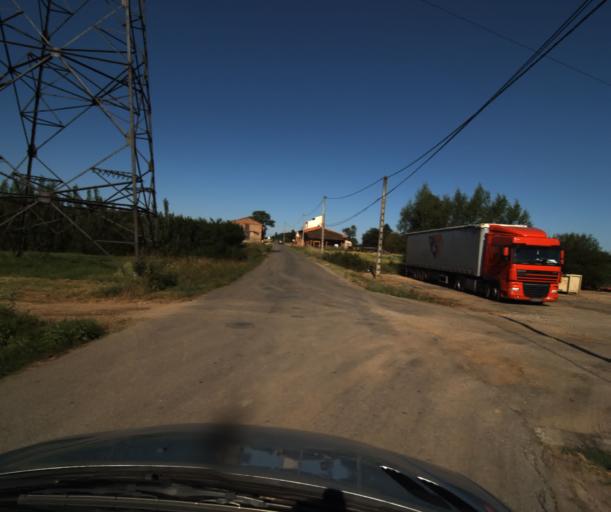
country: FR
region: Midi-Pyrenees
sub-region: Departement du Tarn-et-Garonne
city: Bressols
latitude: 43.9652
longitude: 1.3233
